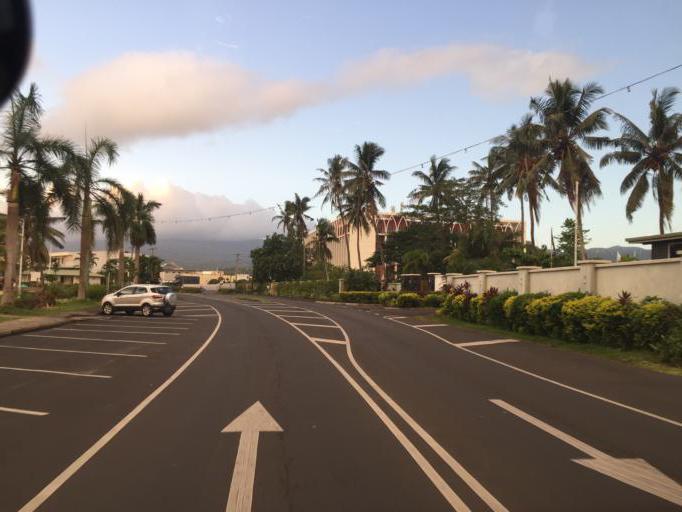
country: WS
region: Tuamasaga
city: Apia
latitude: -13.8271
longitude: -171.7729
